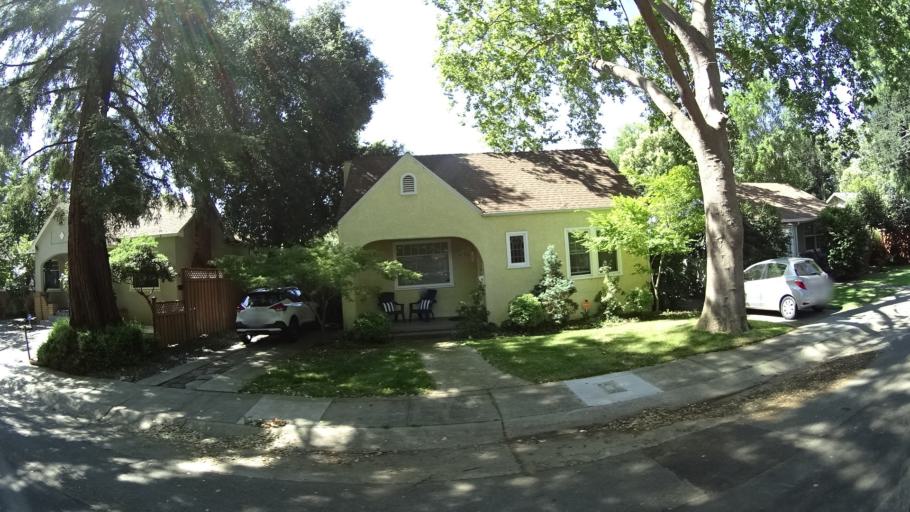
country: US
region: California
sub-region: Sacramento County
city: Sacramento
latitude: 38.5520
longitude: -121.4578
